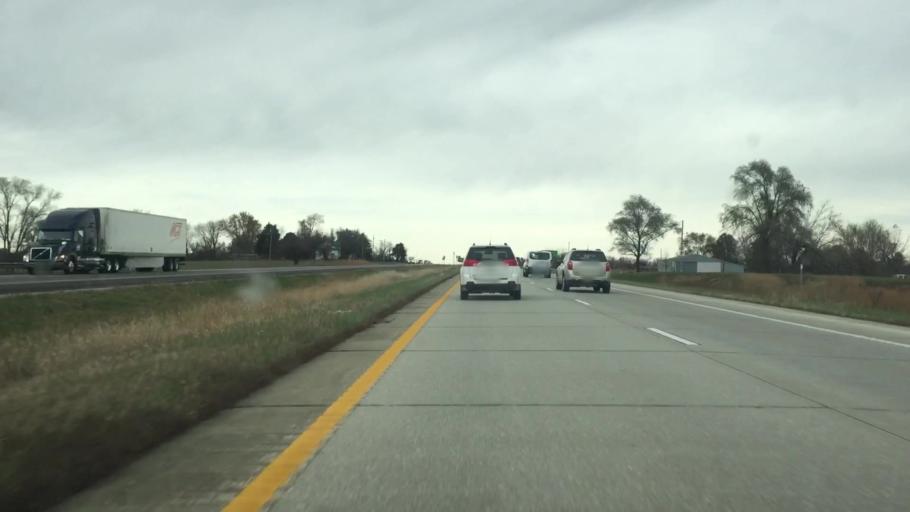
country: US
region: Missouri
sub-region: Saint Clair County
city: Osceola
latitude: 38.1047
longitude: -93.7067
